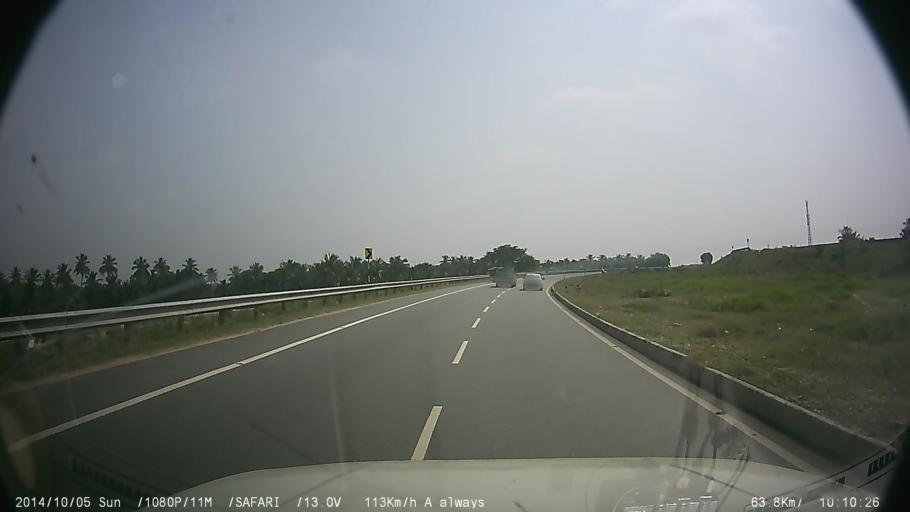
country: IN
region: Tamil Nadu
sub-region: Salem
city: Konganapuram
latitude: 11.5355
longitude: 77.9576
